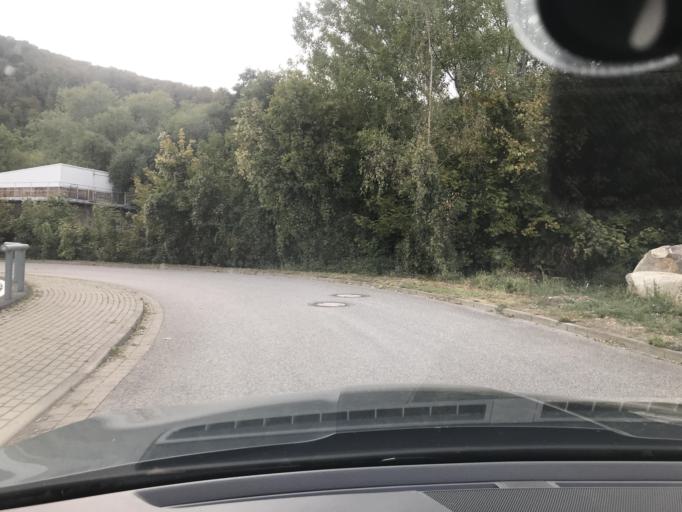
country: DE
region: Saxony-Anhalt
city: Thale
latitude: 51.7478
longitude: 11.0268
